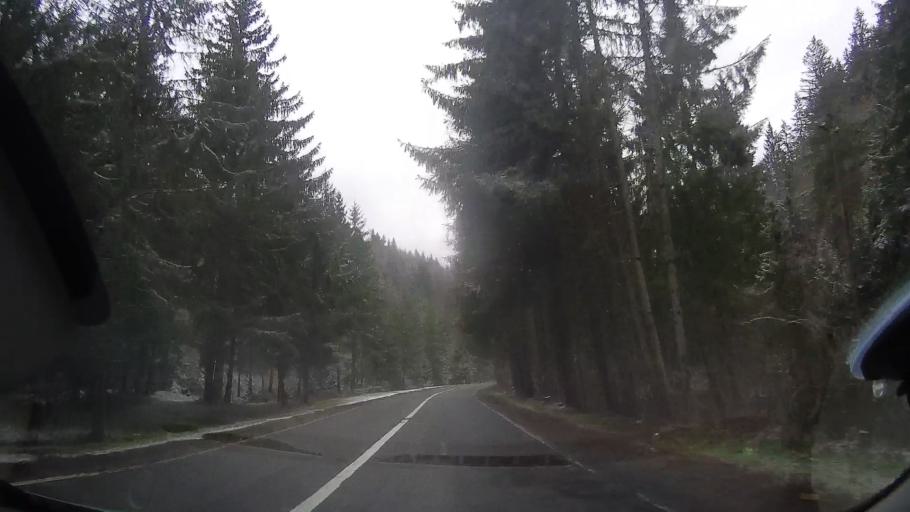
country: RO
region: Cluj
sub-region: Comuna Calatele
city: Calatele
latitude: 46.7398
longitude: 23.0170
